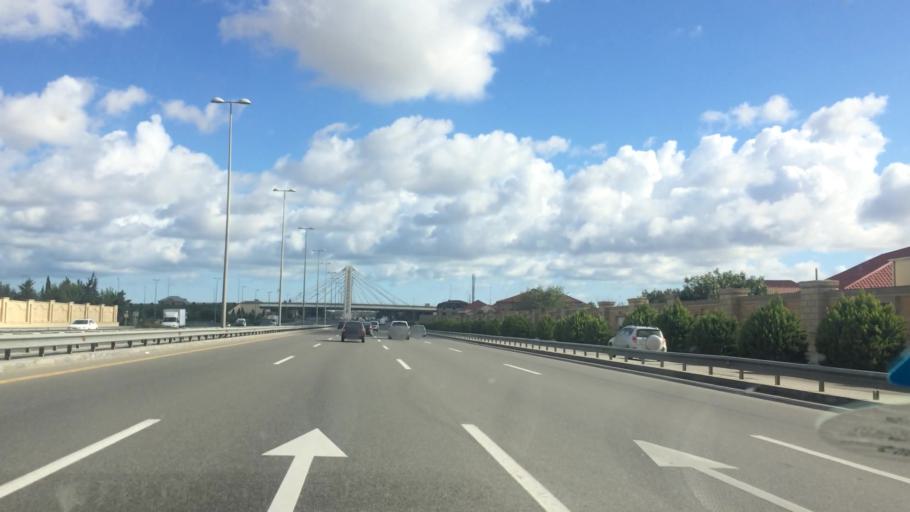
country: AZ
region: Baki
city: Biny Selo
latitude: 40.4569
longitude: 50.0712
